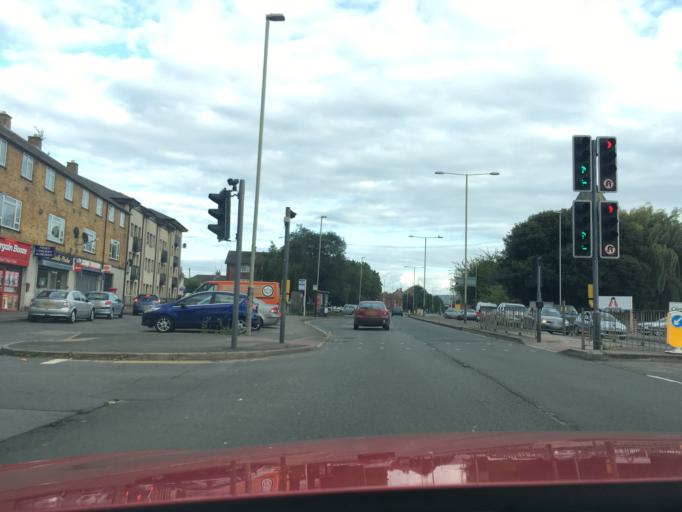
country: GB
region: England
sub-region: Gloucestershire
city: Cheltenham
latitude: 51.9096
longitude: -2.0918
